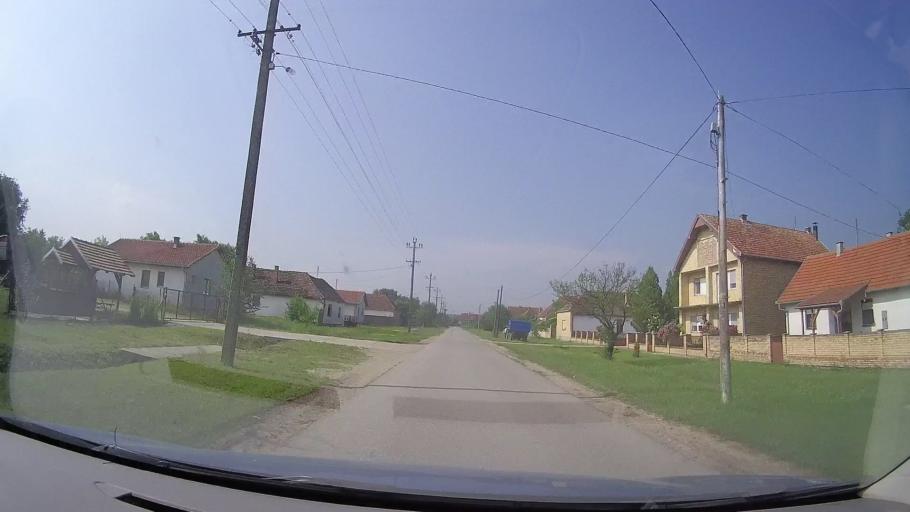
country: RS
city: Jasa Tomic
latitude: 45.4404
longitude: 20.8508
